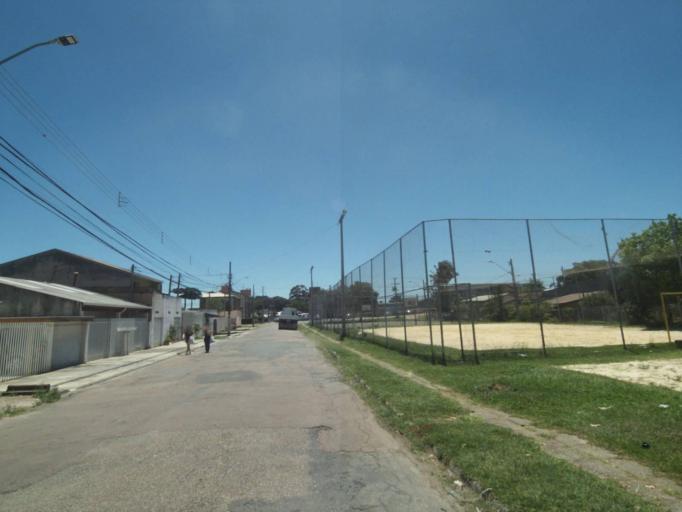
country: BR
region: Parana
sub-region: Curitiba
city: Curitiba
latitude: -25.4798
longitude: -49.3459
